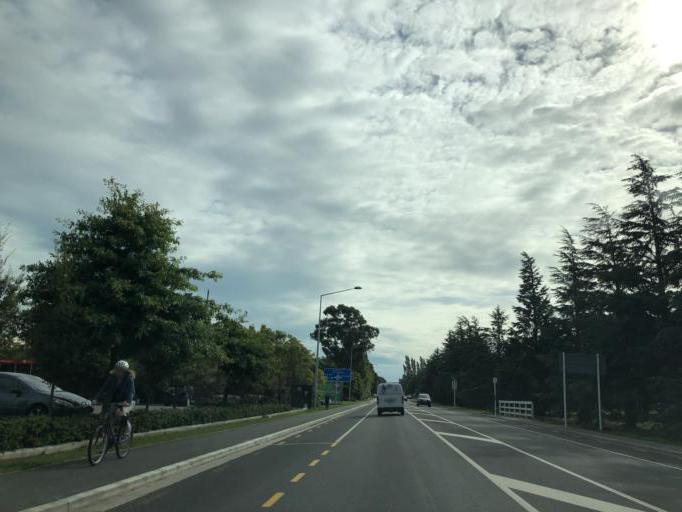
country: NZ
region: Canterbury
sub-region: Selwyn District
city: Lincoln
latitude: -43.6415
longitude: 172.4740
